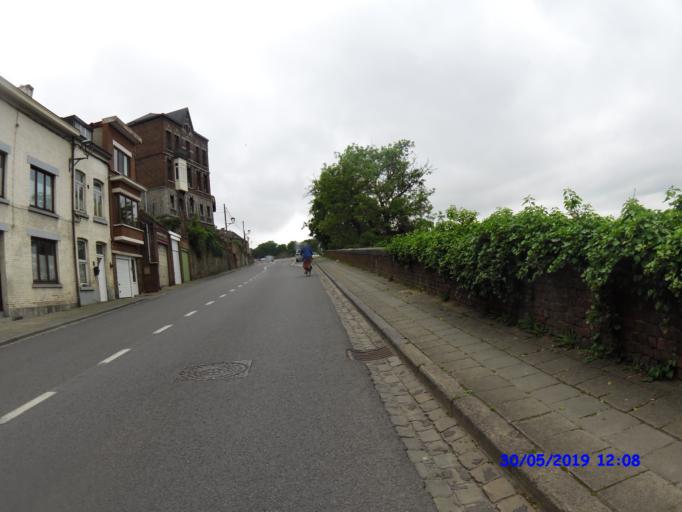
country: BE
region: Wallonia
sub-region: Province du Hainaut
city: Thuin
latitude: 50.3406
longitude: 4.2850
